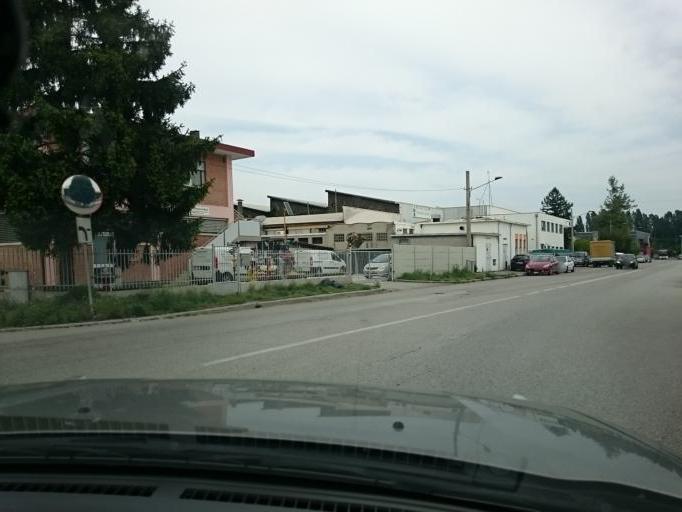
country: IT
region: Veneto
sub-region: Provincia di Padova
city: Noventa
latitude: 45.4119
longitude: 11.9345
